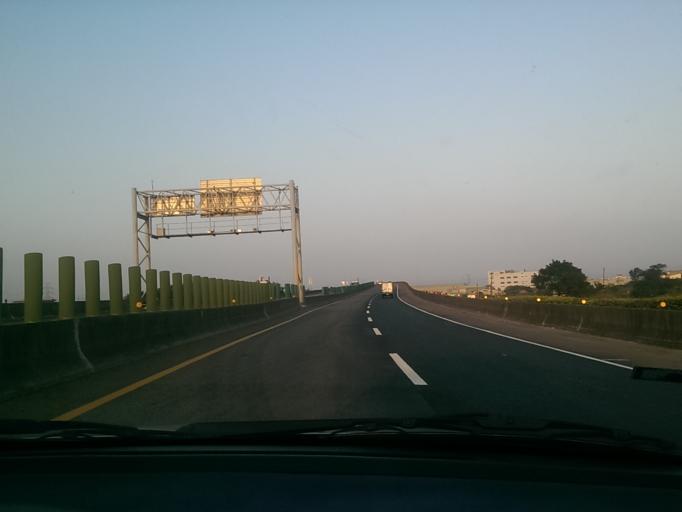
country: TW
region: Taiwan
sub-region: Changhua
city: Chang-hua
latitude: 24.1798
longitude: 120.4837
